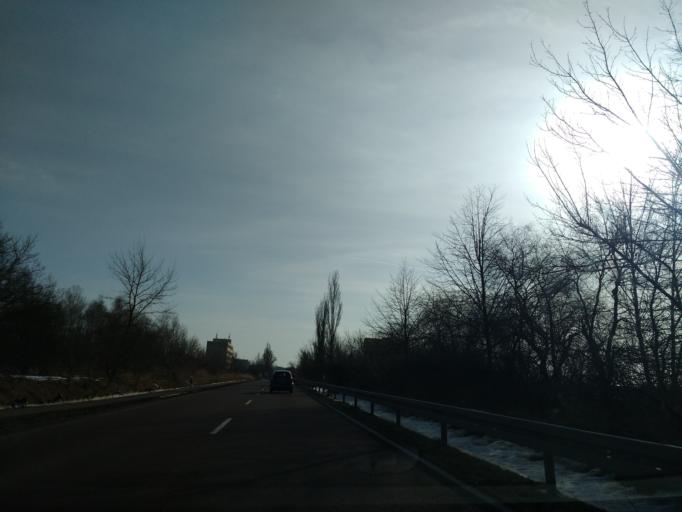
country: DE
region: Saxony-Anhalt
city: Sennewitz
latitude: 51.5309
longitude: 11.9561
